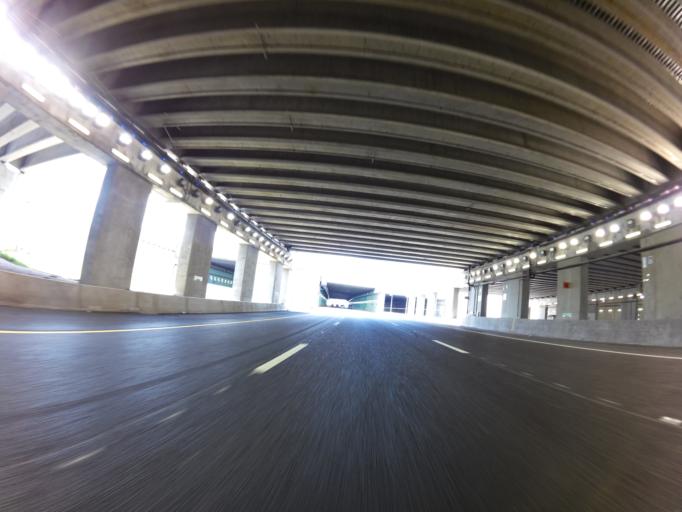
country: US
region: Florida
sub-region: Broward County
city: Dania Beach
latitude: 26.0674
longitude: -80.1382
